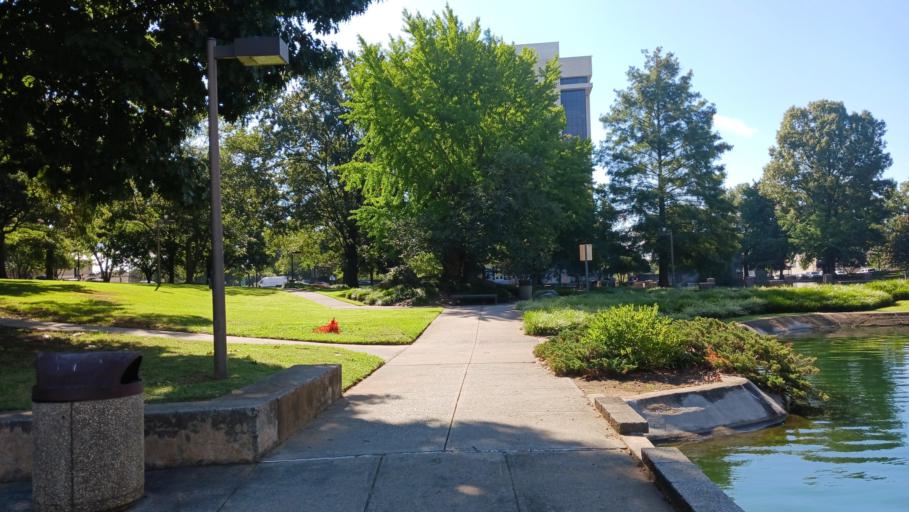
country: US
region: North Carolina
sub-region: Mecklenburg County
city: Charlotte
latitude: 35.2193
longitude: -80.8389
